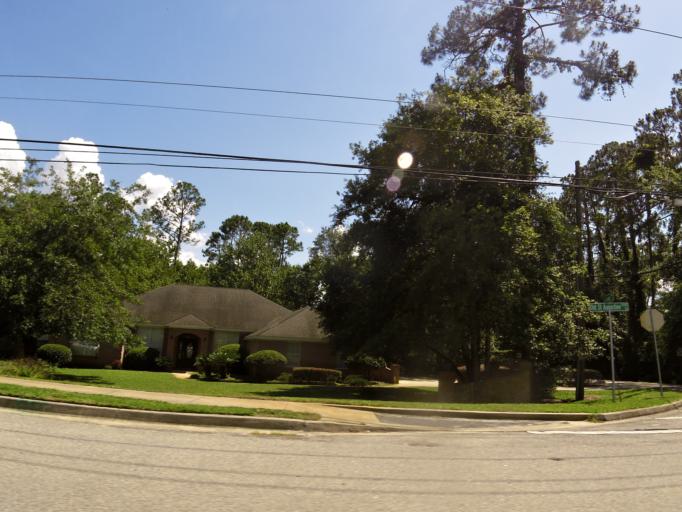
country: US
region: Florida
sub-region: Saint Johns County
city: Fruit Cove
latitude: 30.1562
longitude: -81.5930
